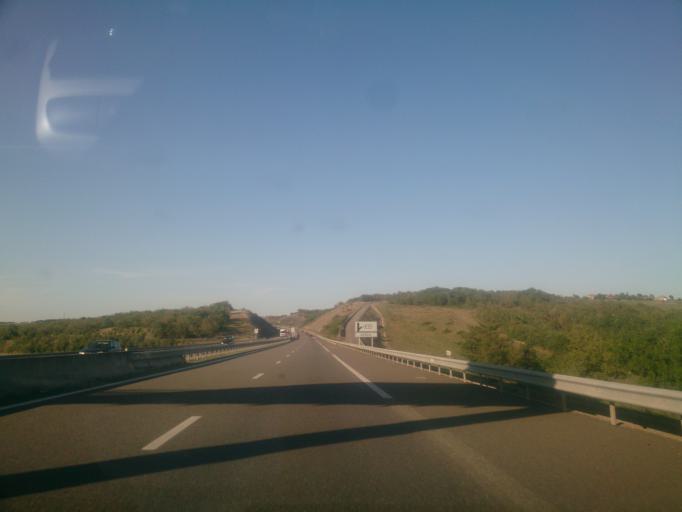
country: FR
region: Midi-Pyrenees
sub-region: Departement du Lot
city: Cahors
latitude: 44.5092
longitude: 1.5007
